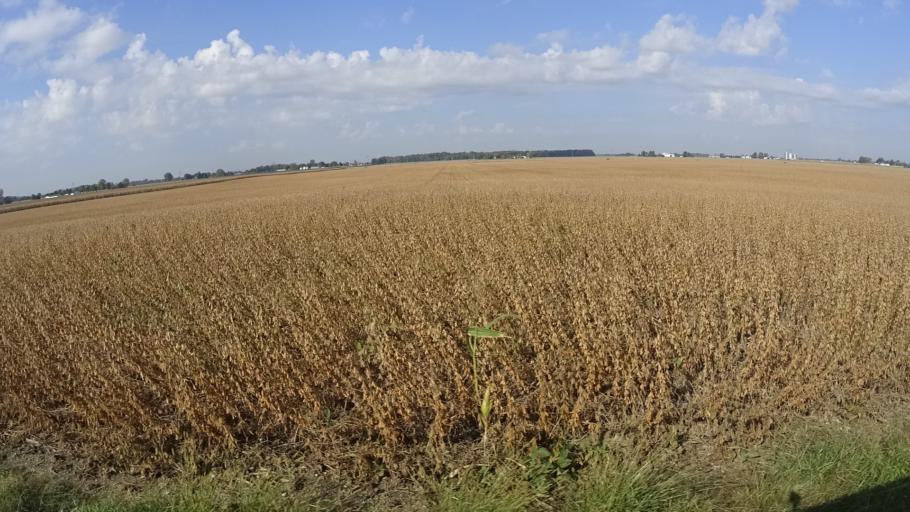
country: US
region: Indiana
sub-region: Madison County
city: Lapel
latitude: 40.0373
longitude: -85.8243
